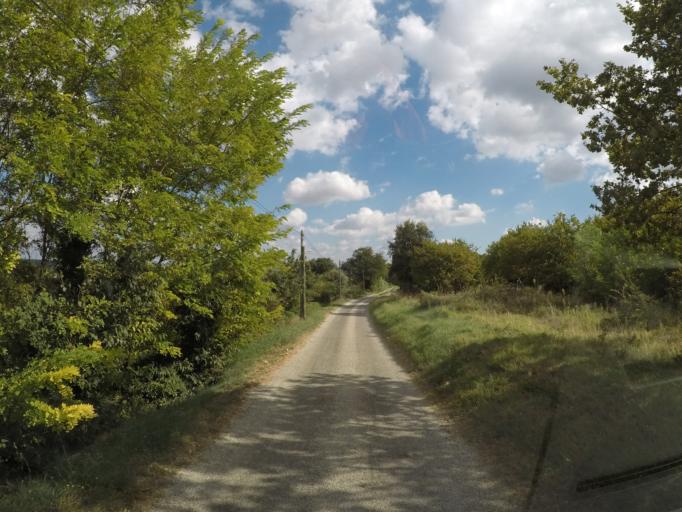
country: FR
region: Rhone-Alpes
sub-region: Departement de la Drome
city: Saint-Restitut
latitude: 44.3045
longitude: 4.7940
